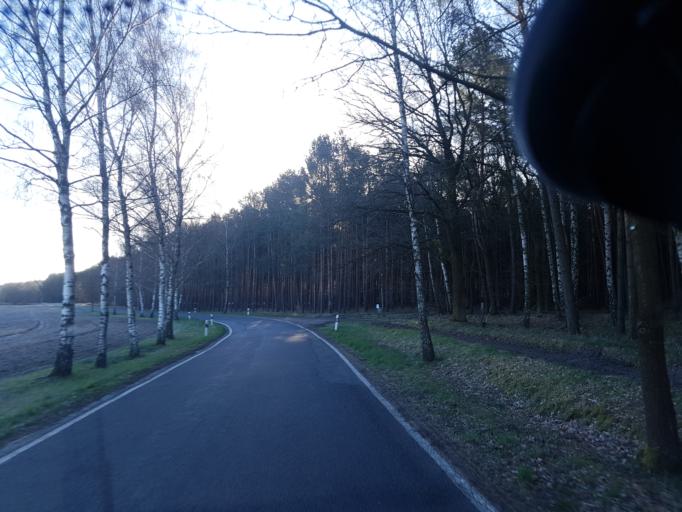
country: DE
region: Brandenburg
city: Jamlitz
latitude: 52.0326
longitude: 14.3554
